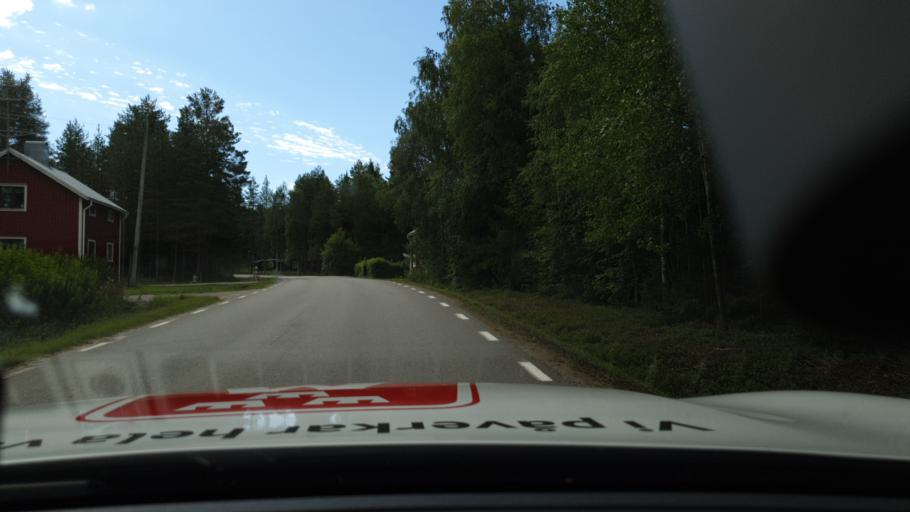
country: SE
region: Norrbotten
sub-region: Kalix Kommun
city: Toere
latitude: 65.8487
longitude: 22.6780
